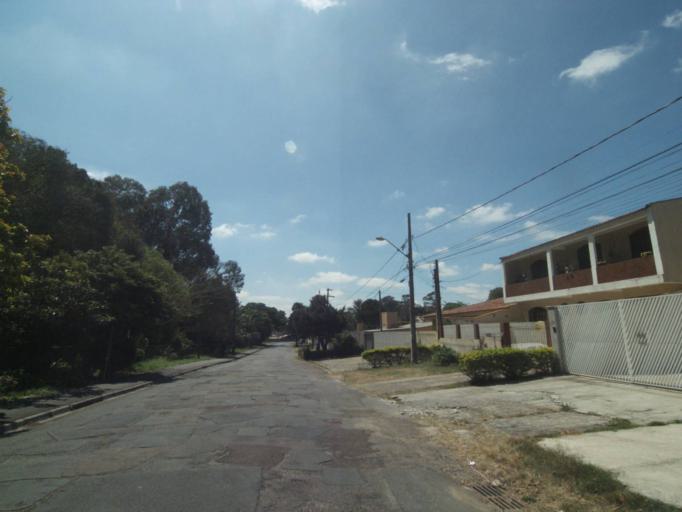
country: BR
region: Parana
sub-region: Sao Jose Dos Pinhais
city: Sao Jose dos Pinhais
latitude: -25.5093
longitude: -49.2413
